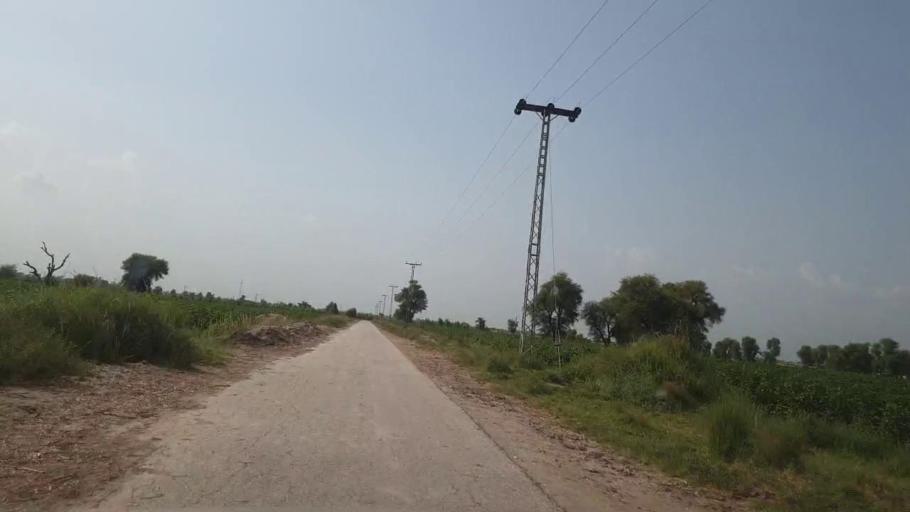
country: PK
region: Sindh
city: Pano Aqil
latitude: 27.7871
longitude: 69.1564
